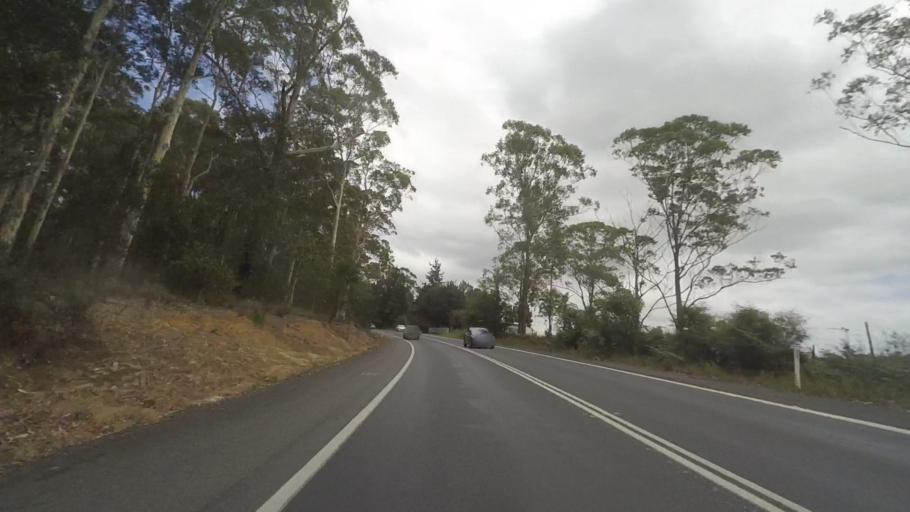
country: AU
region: New South Wales
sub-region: Shoalhaven Shire
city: Falls Creek
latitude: -35.0813
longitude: 150.5186
